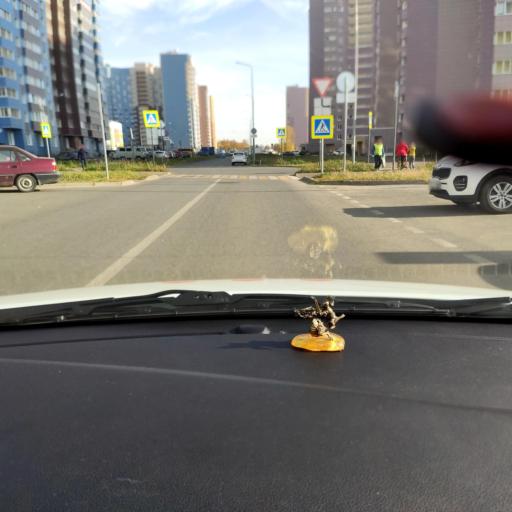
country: RU
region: Tatarstan
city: Osinovo
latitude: 55.8638
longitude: 48.8764
